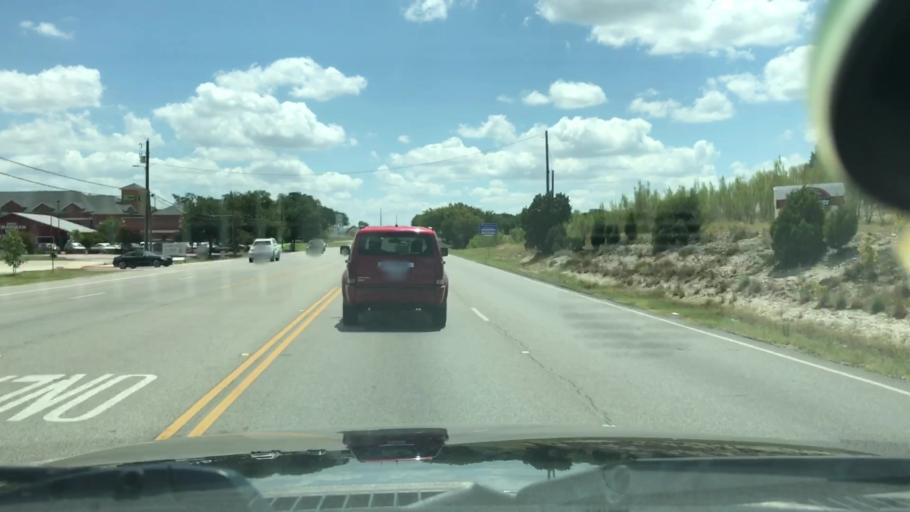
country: US
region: Texas
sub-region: Williamson County
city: Cedar Park
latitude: 30.5001
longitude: -97.8162
